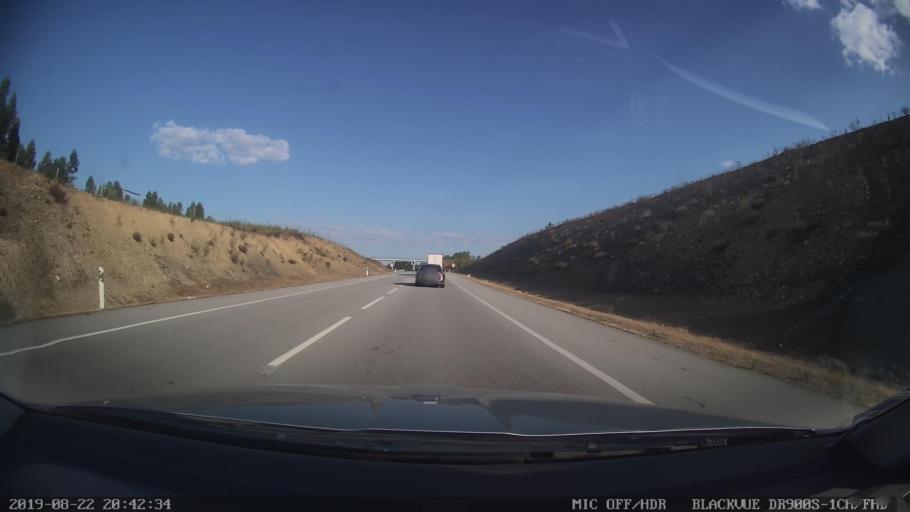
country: PT
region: Castelo Branco
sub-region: Proenca-A-Nova
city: Proenca-a-Nova
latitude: 39.6954
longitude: -7.8183
